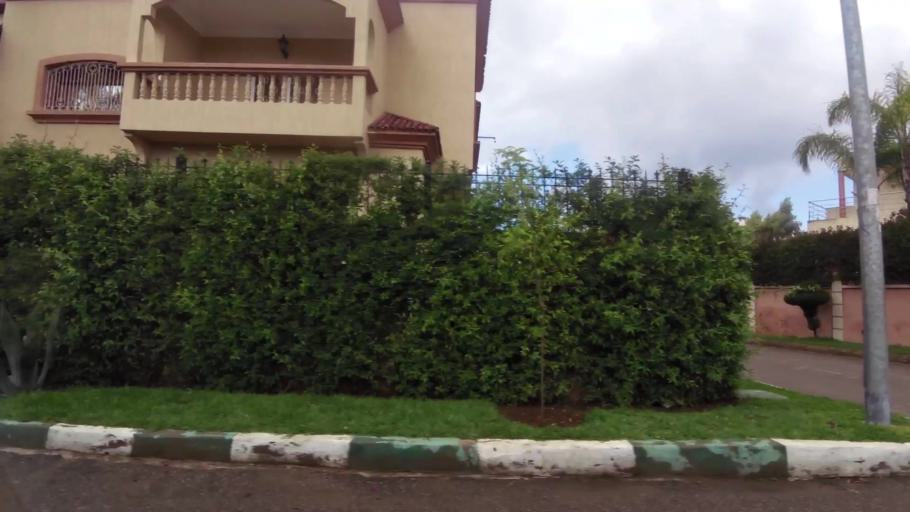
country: MA
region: Grand Casablanca
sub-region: Nouaceur
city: Bouskoura
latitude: 33.5162
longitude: -7.6393
